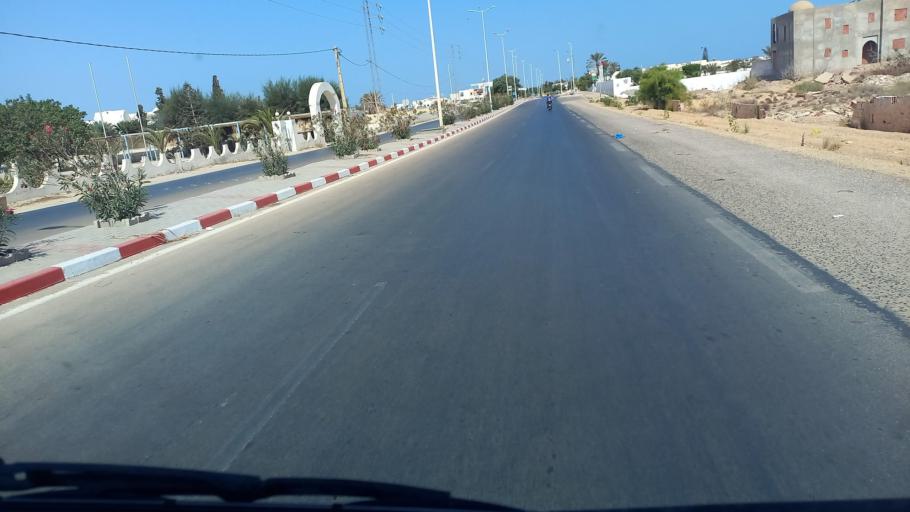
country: TN
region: Madanin
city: Midoun
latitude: 33.8567
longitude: 10.9769
